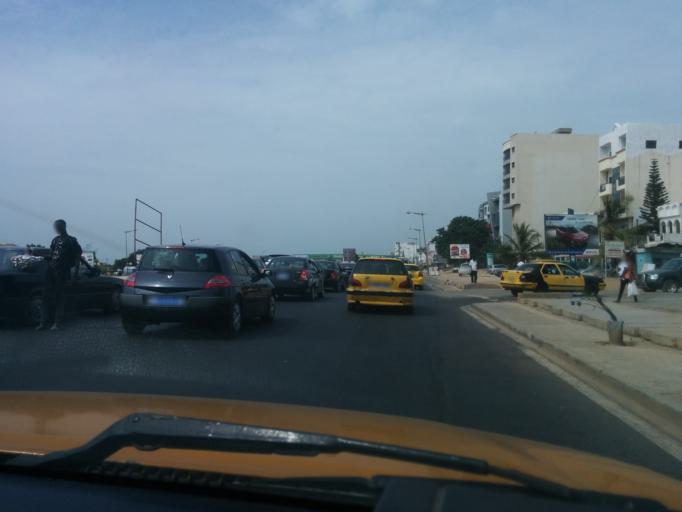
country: SN
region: Dakar
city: Mermoz Boabab
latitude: 14.7248
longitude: -17.4711
